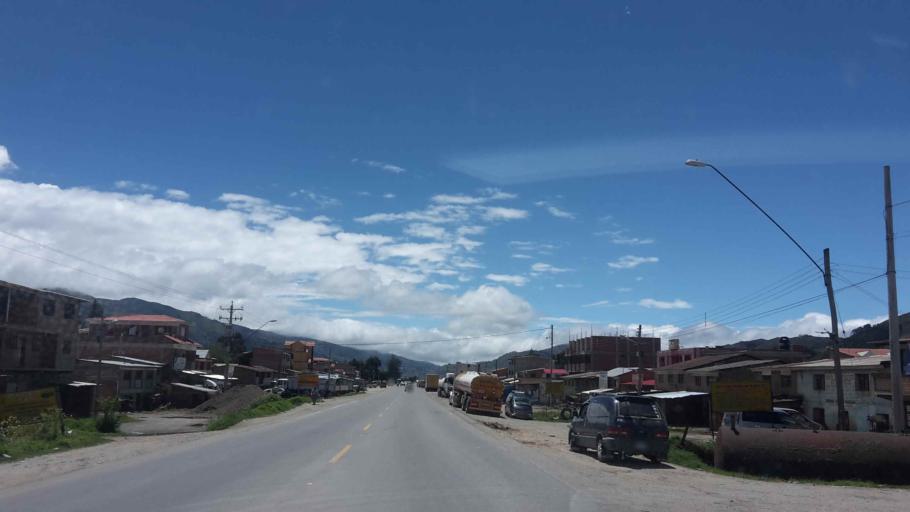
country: BO
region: Cochabamba
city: Colomi
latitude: -17.3340
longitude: -65.8687
